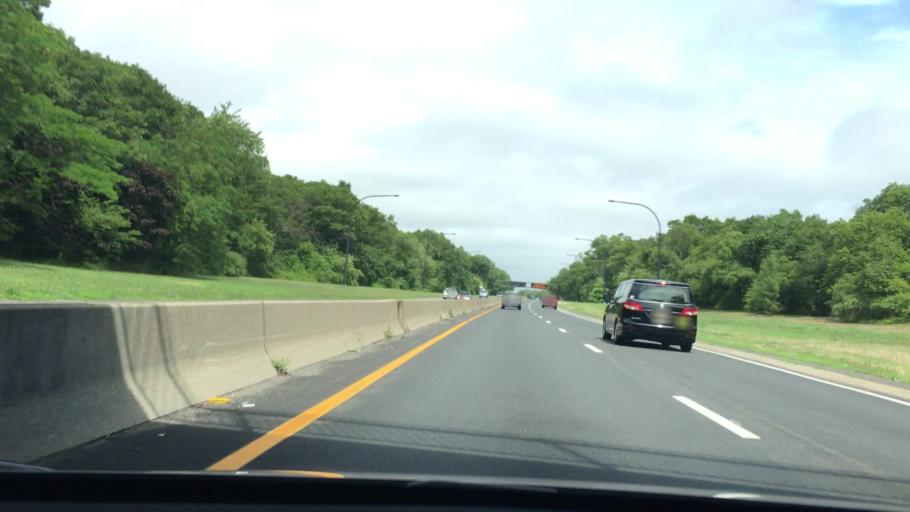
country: US
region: New York
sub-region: Nassau County
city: North Bellmore
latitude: 40.7079
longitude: -73.5263
